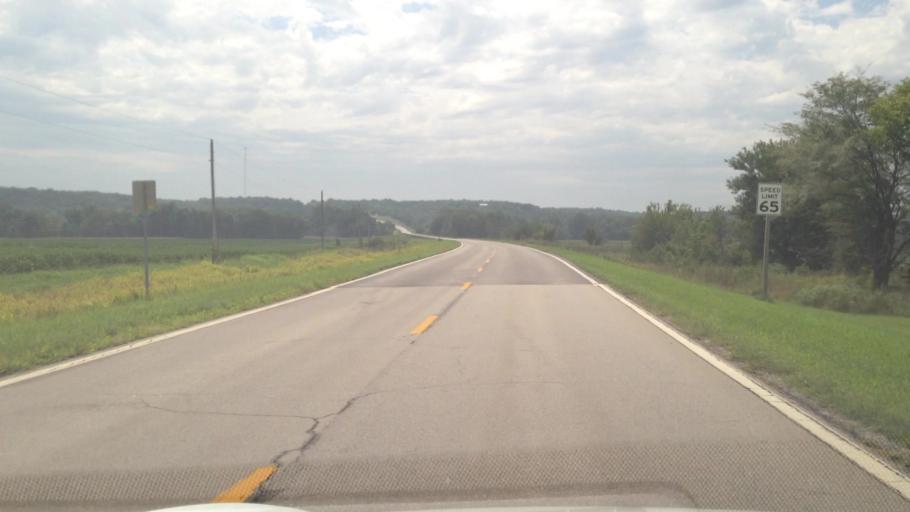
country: US
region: Kansas
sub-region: Bourbon County
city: Fort Scott
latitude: 37.8437
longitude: -94.9811
